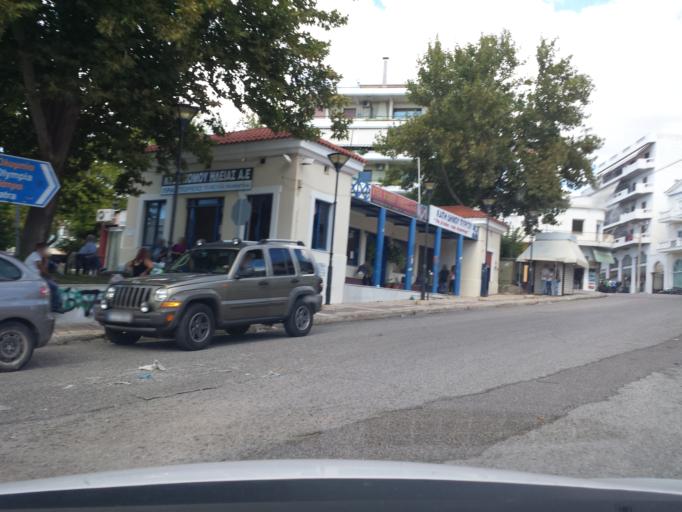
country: GR
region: West Greece
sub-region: Nomos Ileias
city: Pyrgos
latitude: 37.6701
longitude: 21.4471
